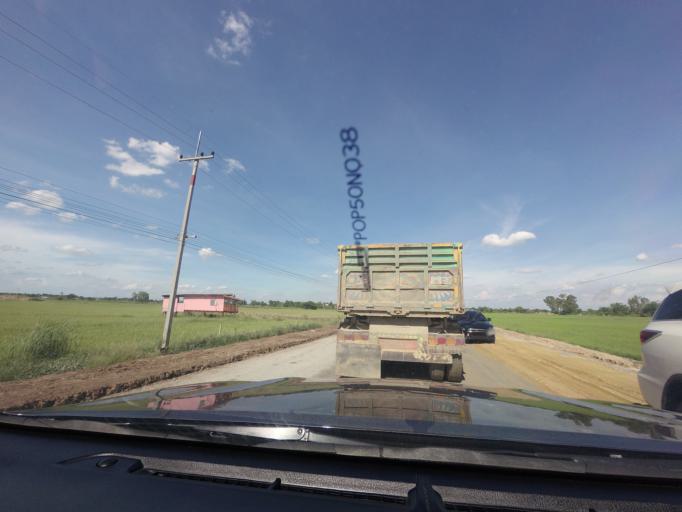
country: TH
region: Suphan Buri
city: Song Phi Nong
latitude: 14.1793
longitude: 100.0406
